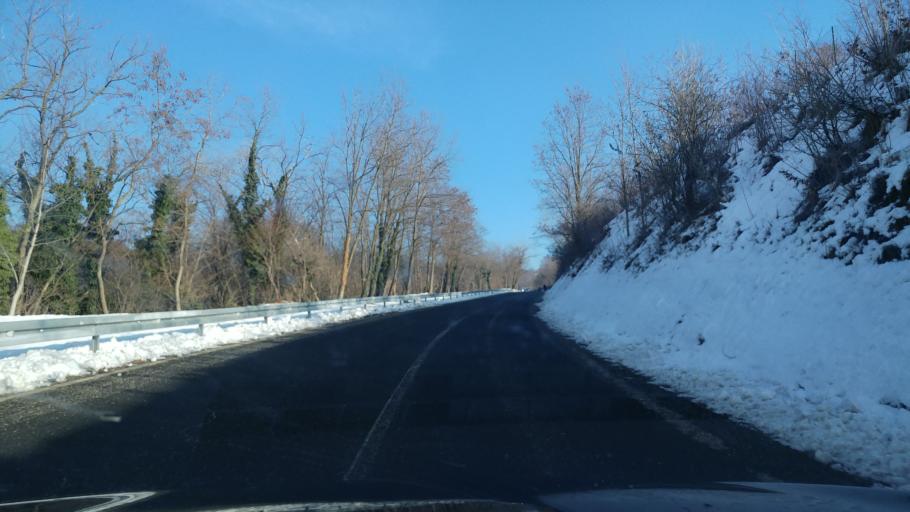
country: HR
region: Grad Zagreb
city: Stenjevec
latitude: 45.8316
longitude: 15.8748
